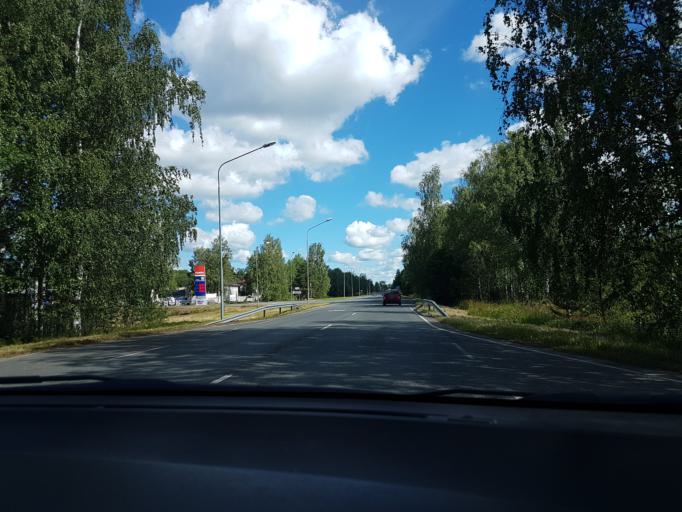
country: FI
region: Uusimaa
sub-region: Helsinki
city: Kerava
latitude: 60.3901
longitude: 25.1004
